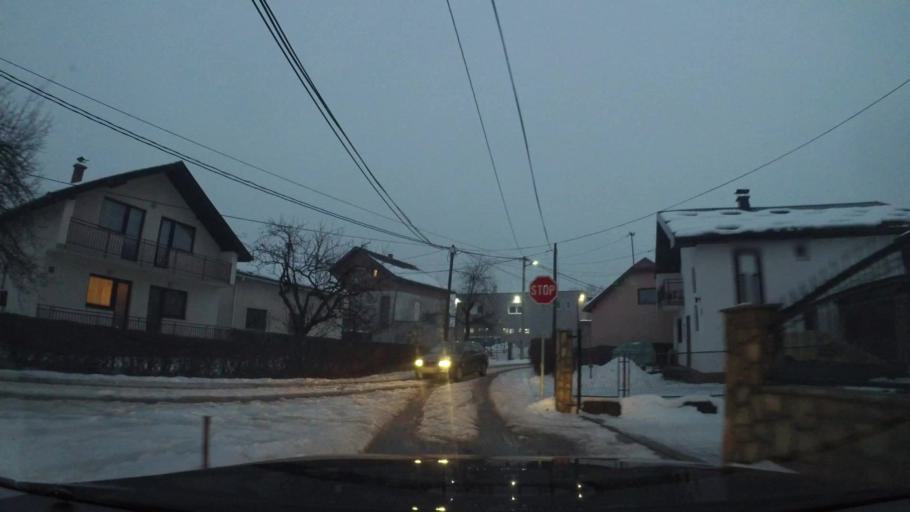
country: BA
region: Federation of Bosnia and Herzegovina
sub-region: Kanton Sarajevo
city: Sarajevo
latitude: 43.8533
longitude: 18.2943
